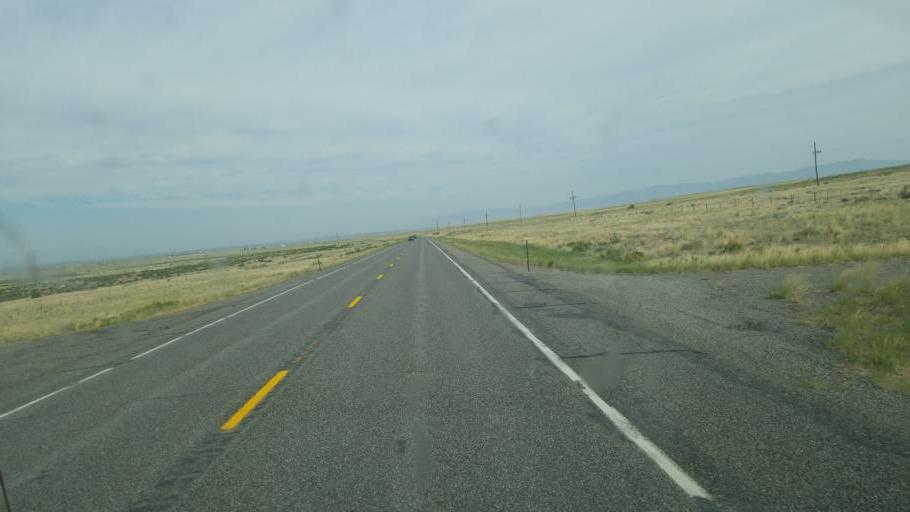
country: US
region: Wyoming
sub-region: Fremont County
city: Riverton
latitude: 43.2299
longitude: -108.0590
